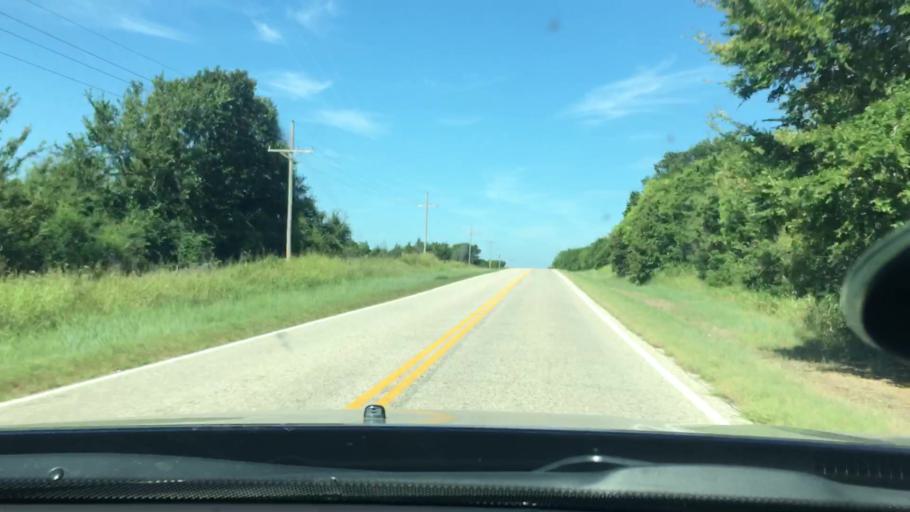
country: US
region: Oklahoma
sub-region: Johnston County
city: Tishomingo
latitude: 34.3614
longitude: -96.5552
